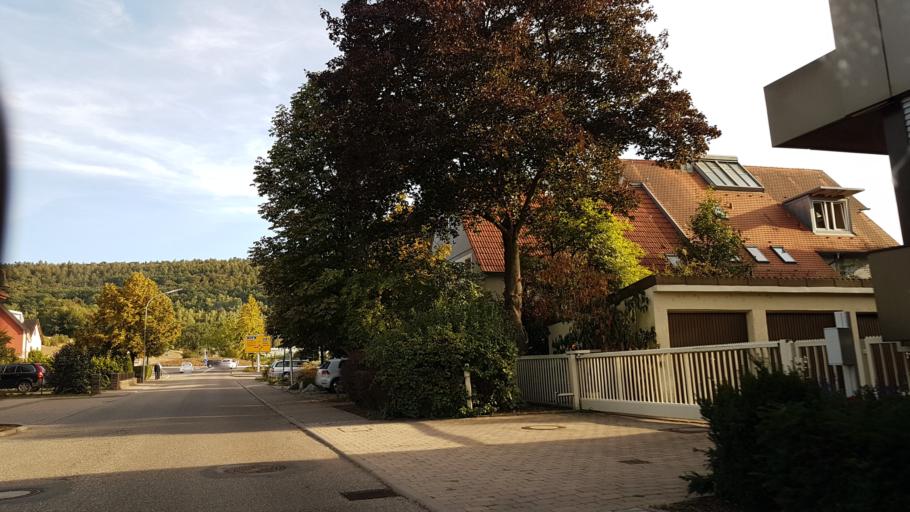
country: DE
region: Baden-Wuerttemberg
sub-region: Regierungsbezirk Stuttgart
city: Eberstadt
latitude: 49.1771
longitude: 9.3220
